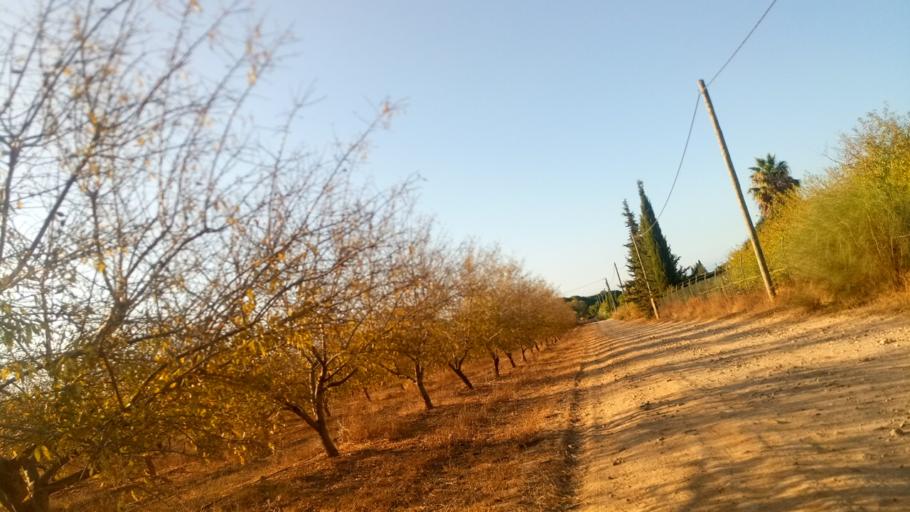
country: PT
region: Faro
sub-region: Tavira
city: Tavira
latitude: 37.1461
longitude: -7.5835
